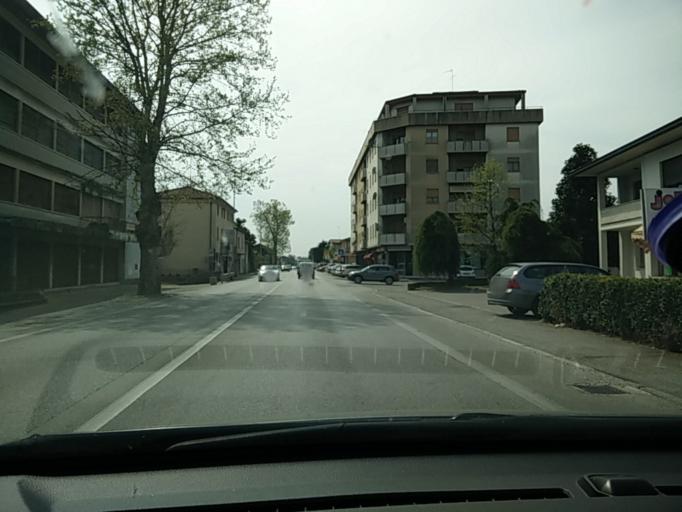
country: IT
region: Veneto
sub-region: Provincia di Treviso
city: San Fior di Sopra
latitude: 45.9207
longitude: 12.3565
